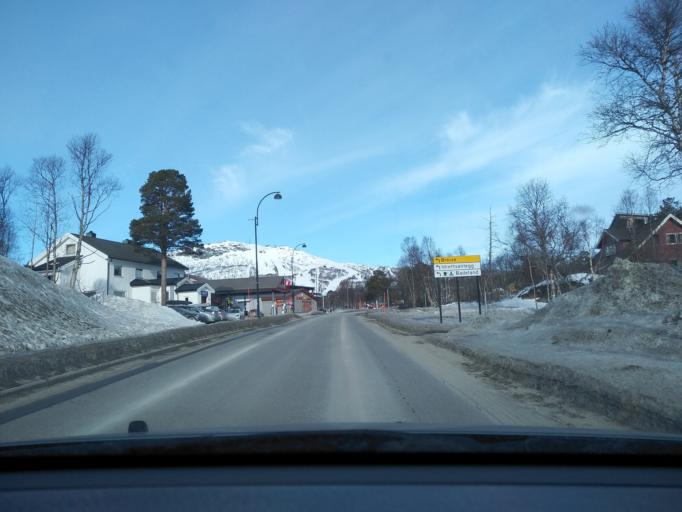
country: NO
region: Aust-Agder
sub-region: Bykle
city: Hovden
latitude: 59.5586
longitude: 7.3573
